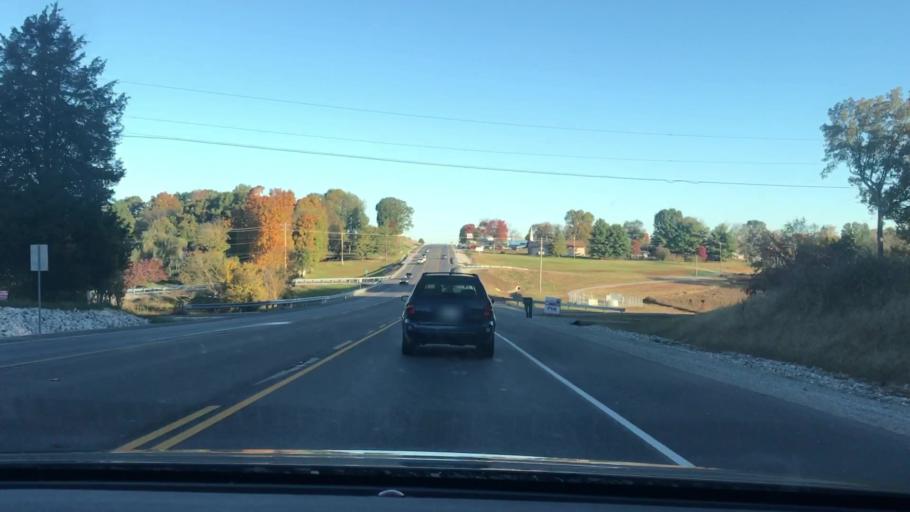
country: US
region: Kentucky
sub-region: Simpson County
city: Franklin
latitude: 36.6863
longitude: -86.5681
